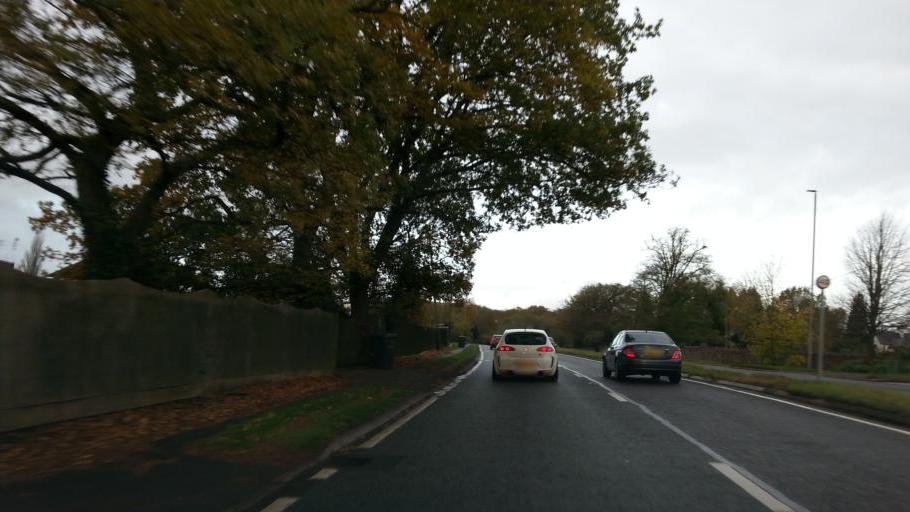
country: GB
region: England
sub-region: Leicestershire
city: Markfield
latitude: 52.6748
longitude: -1.2521
